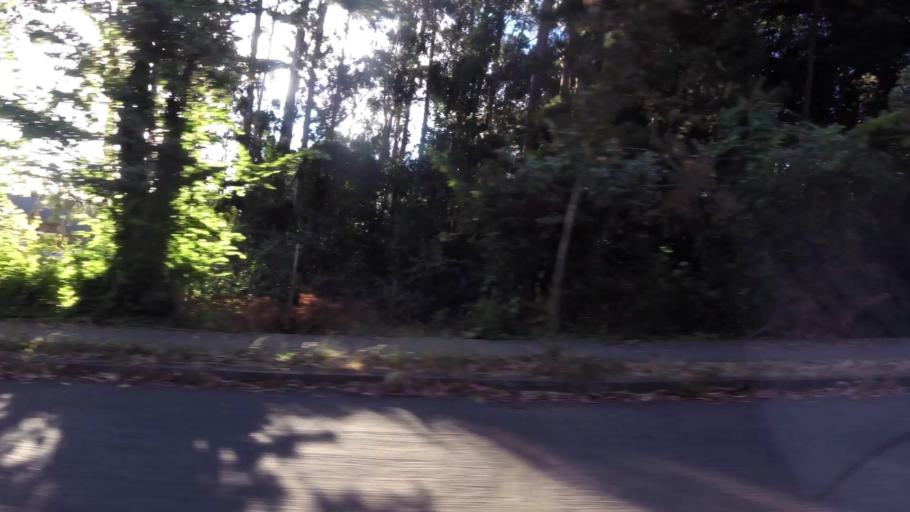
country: CL
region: Biobio
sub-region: Provincia de Concepcion
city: Concepcion
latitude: -36.8578
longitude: -73.0965
